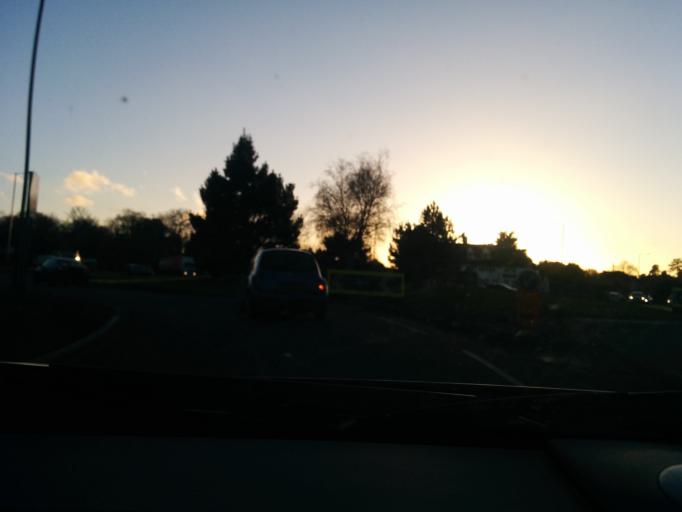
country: GB
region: England
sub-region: Buckinghamshire
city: Denham
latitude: 51.5358
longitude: -0.5292
